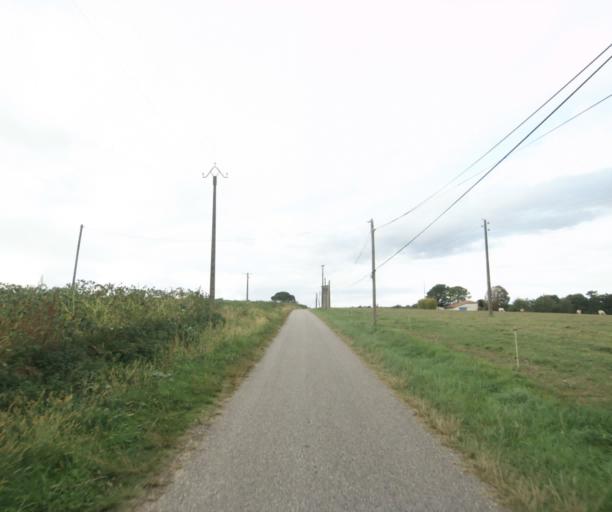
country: FR
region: Midi-Pyrenees
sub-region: Departement du Gers
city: Eauze
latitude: 43.9403
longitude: 0.0816
